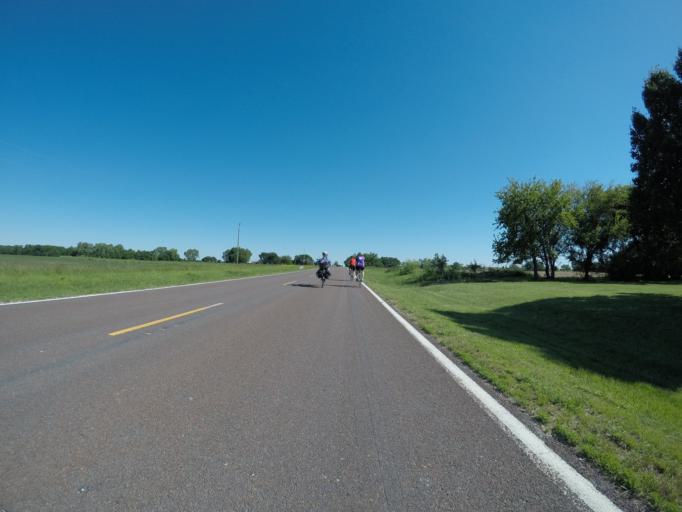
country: US
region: Kansas
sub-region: Osage County
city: Osage City
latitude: 38.7249
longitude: -96.0939
